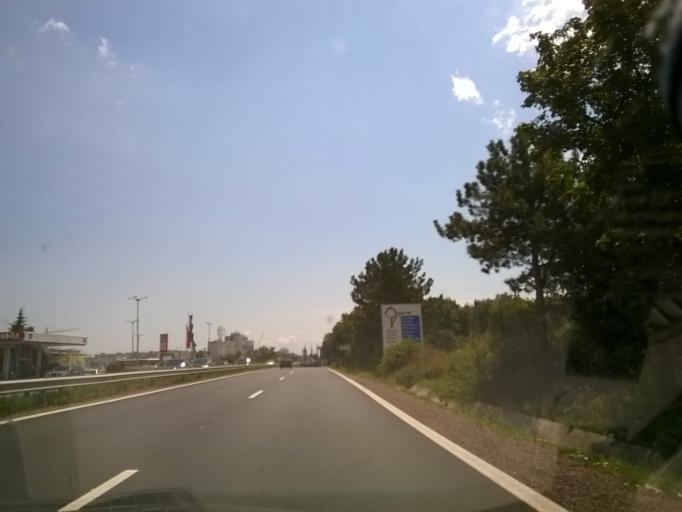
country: BG
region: Burgas
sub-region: Obshtina Burgas
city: Burgas
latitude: 42.5312
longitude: 27.4485
